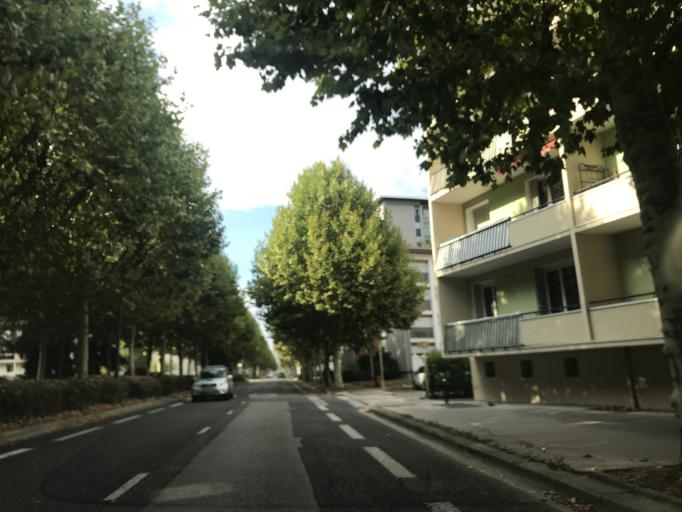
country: FR
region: Rhone-Alpes
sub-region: Departement de la Haute-Savoie
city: Annecy-le-Vieux
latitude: 45.9135
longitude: 6.1349
